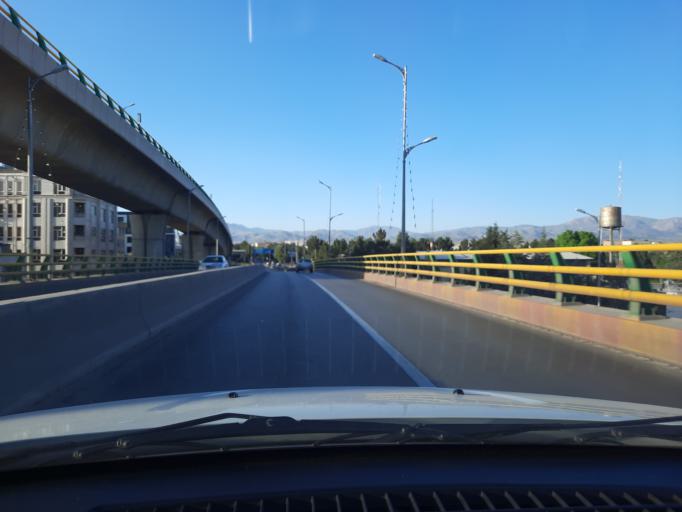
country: IR
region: Qazvin
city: Qazvin
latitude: 36.2748
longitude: 50.0238
